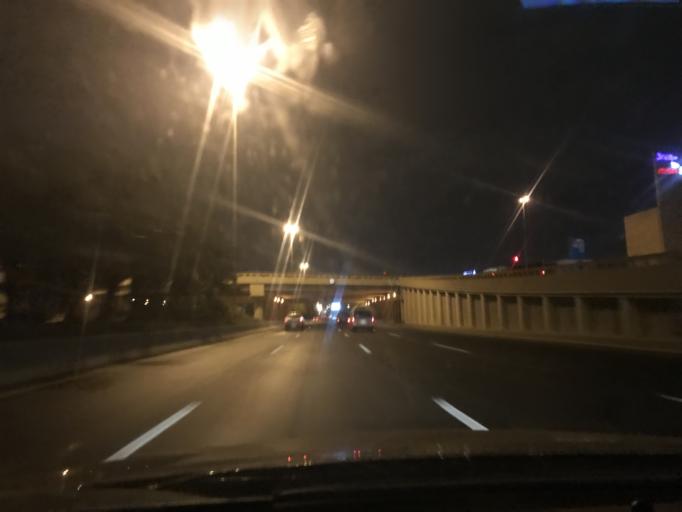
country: SA
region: Ar Riyad
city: Riyadh
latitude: 24.7478
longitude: 46.6161
